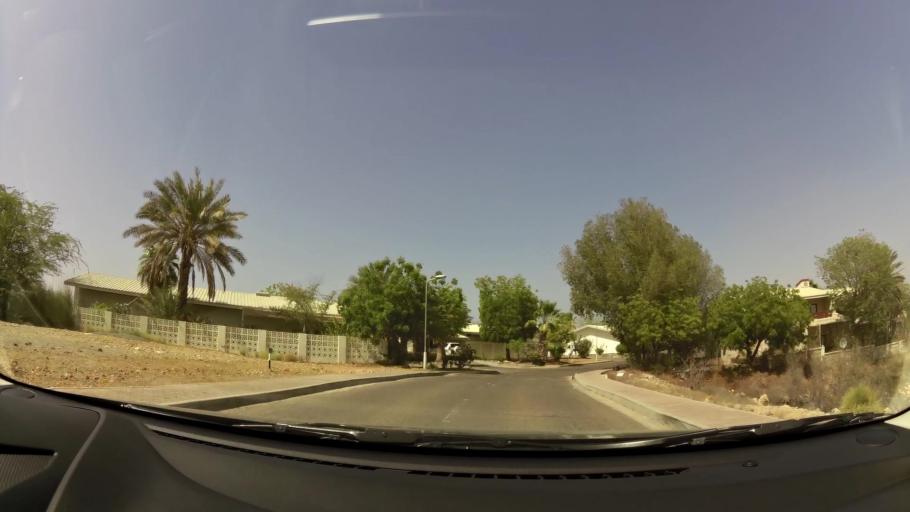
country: OM
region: Muhafazat Masqat
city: Muscat
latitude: 23.6278
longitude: 58.4926
